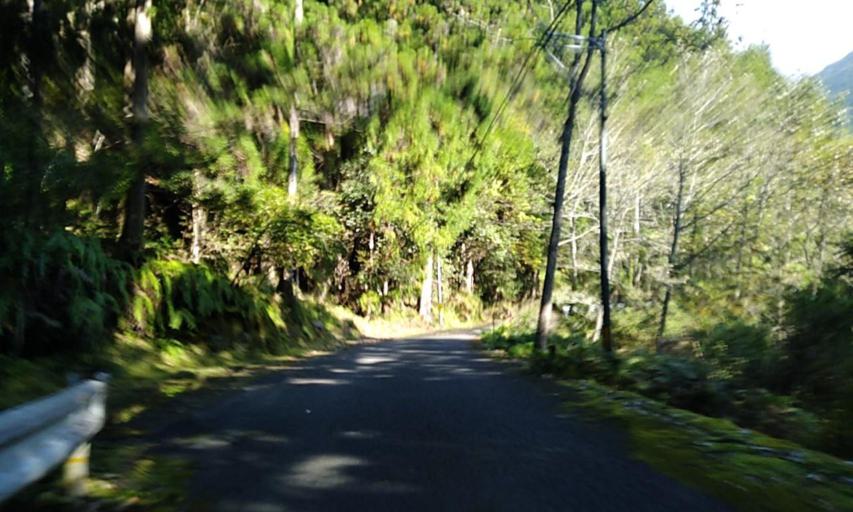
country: JP
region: Wakayama
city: Shingu
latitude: 33.9112
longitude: 135.9880
